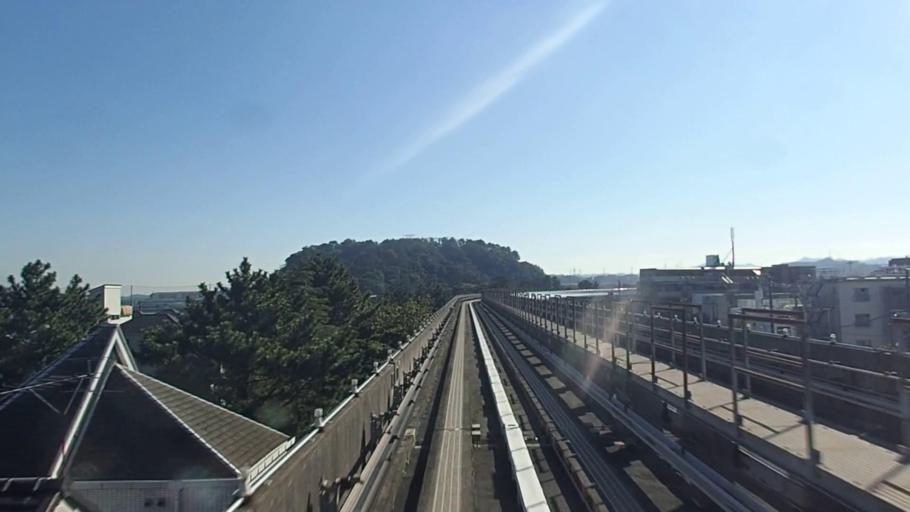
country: JP
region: Kanagawa
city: Yokosuka
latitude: 35.3336
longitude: 139.6330
